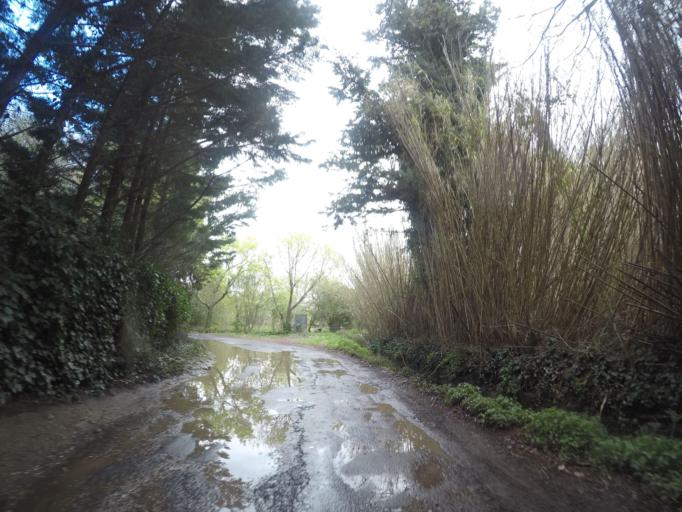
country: FR
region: Languedoc-Roussillon
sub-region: Departement des Pyrenees-Orientales
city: Pezilla-la-Riviere
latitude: 42.6887
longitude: 2.7786
